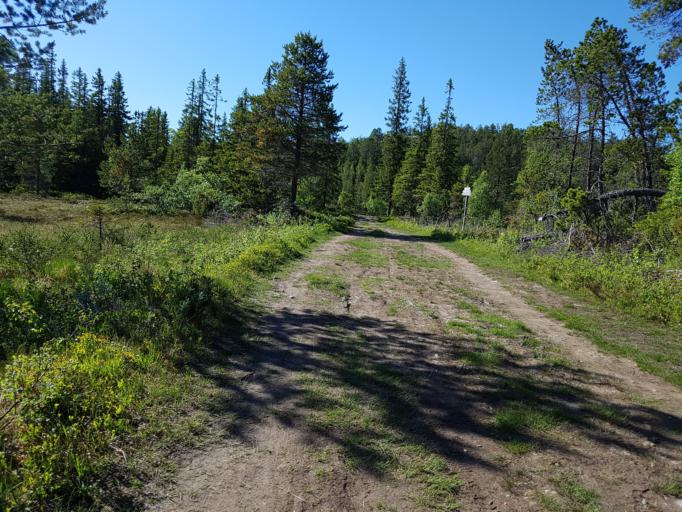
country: NO
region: Sor-Trondelag
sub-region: Trondheim
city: Trondheim
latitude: 63.4284
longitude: 10.2929
